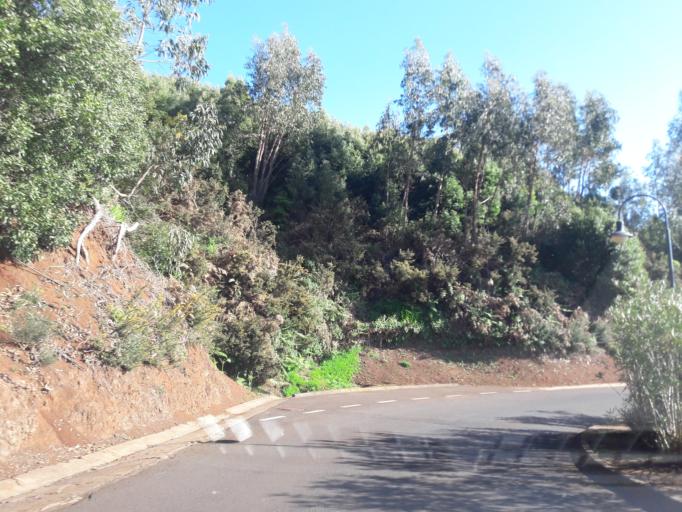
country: PT
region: Madeira
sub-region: Funchal
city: Nossa Senhora do Monte
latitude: 32.6562
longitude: -16.8719
